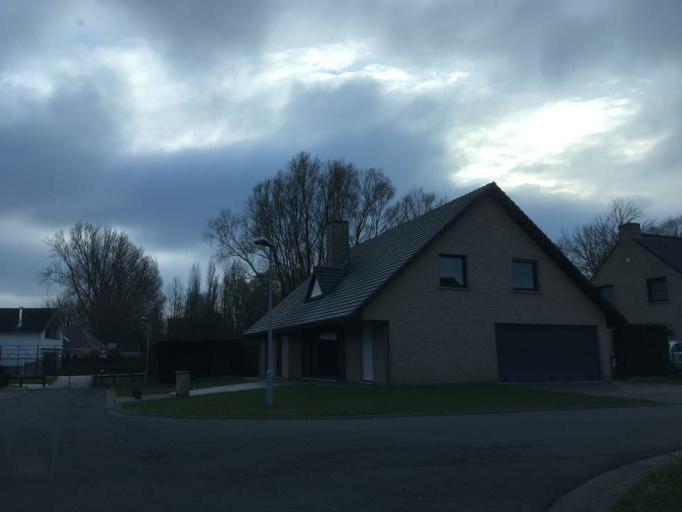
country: BE
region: Flanders
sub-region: Provincie West-Vlaanderen
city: Roeselare
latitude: 50.9466
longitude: 3.1084
